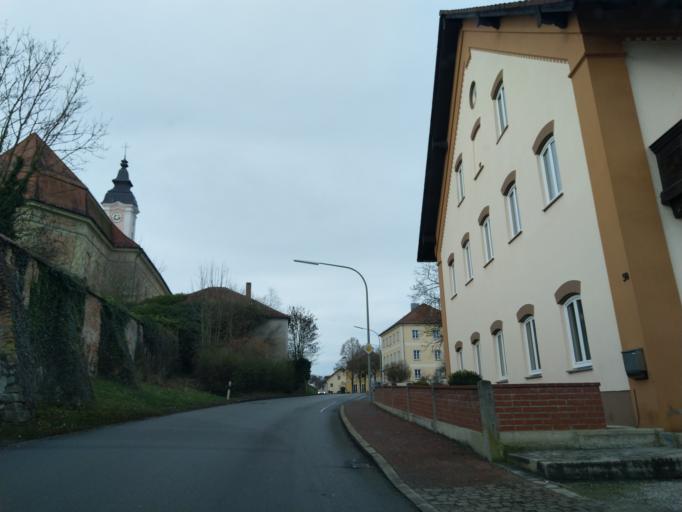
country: DE
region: Bavaria
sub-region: Lower Bavaria
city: Osterhofen
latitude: 48.6916
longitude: 13.0169
